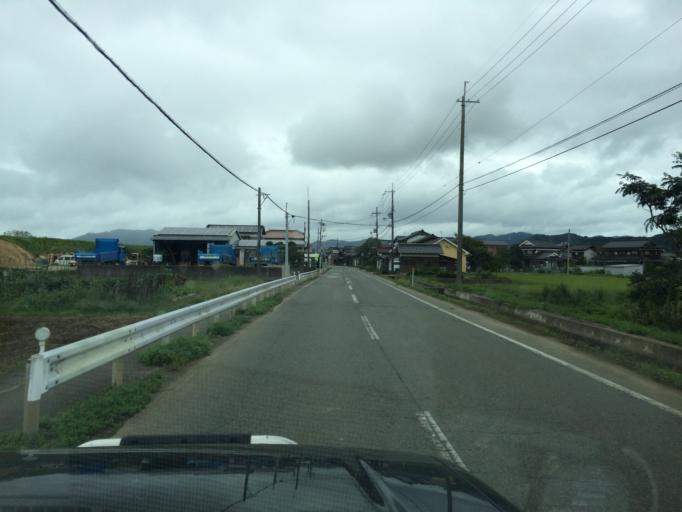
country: JP
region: Hyogo
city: Toyooka
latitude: 35.5079
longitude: 134.8238
